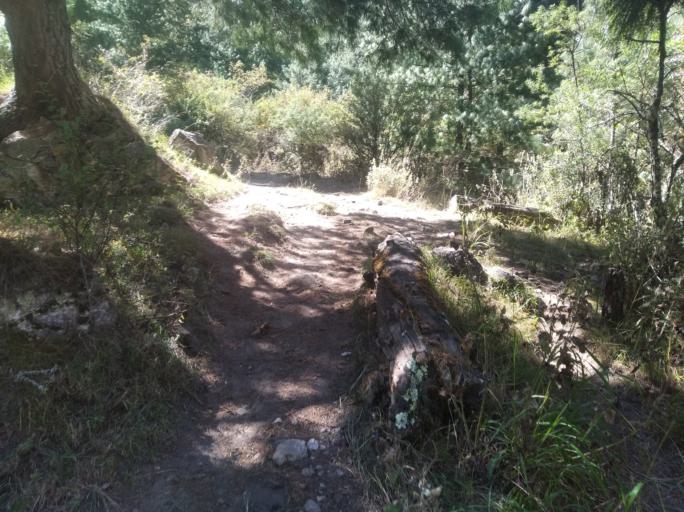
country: NP
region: Western Region
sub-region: Dhawalagiri Zone
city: Jomsom
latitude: 28.8891
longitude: 83.0718
